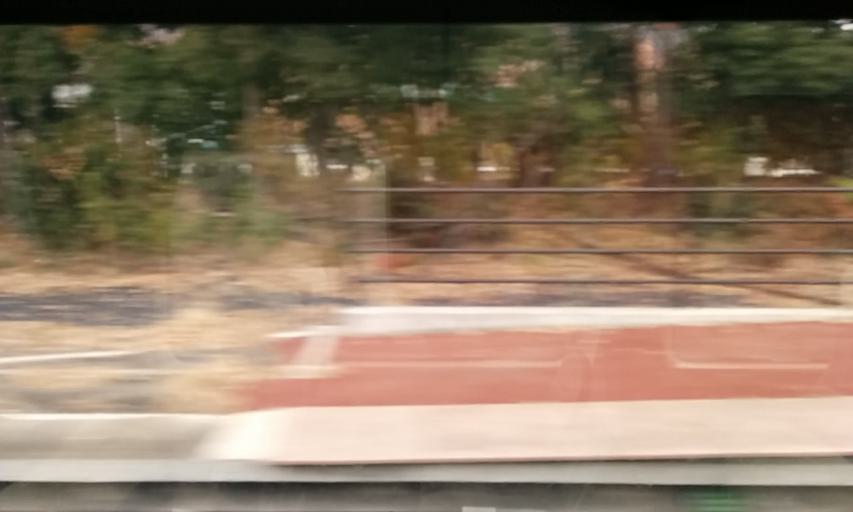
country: JP
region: Nagano
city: Nagano-shi
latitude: 36.5522
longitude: 138.1074
